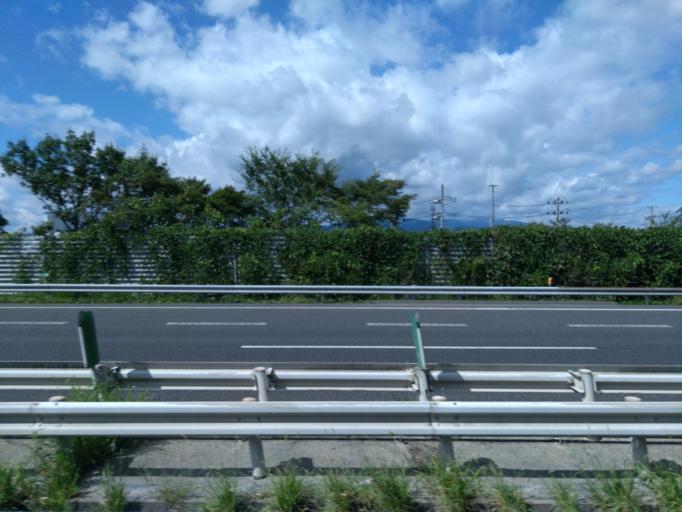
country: JP
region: Miyagi
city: Tomiya
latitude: 38.4387
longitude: 140.9156
